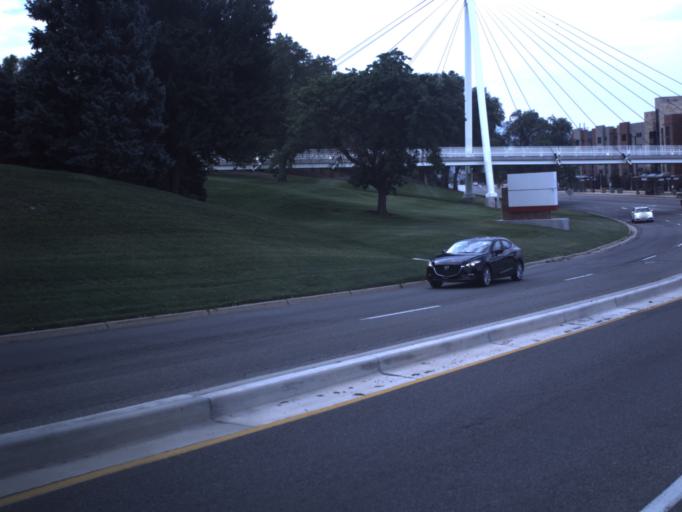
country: US
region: Utah
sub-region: Salt Lake County
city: Salt Lake City
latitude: 40.7663
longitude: -111.8368
